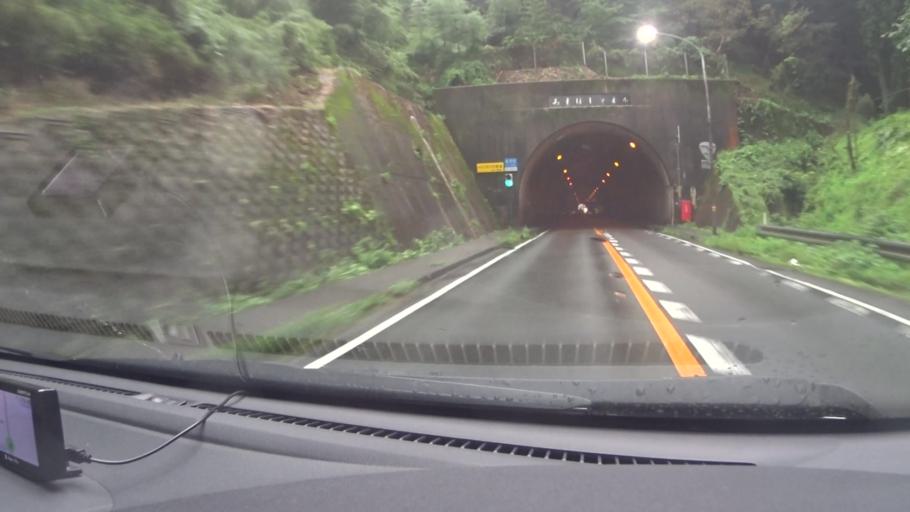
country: JP
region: Kyoto
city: Ayabe
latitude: 35.2416
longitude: 135.3155
